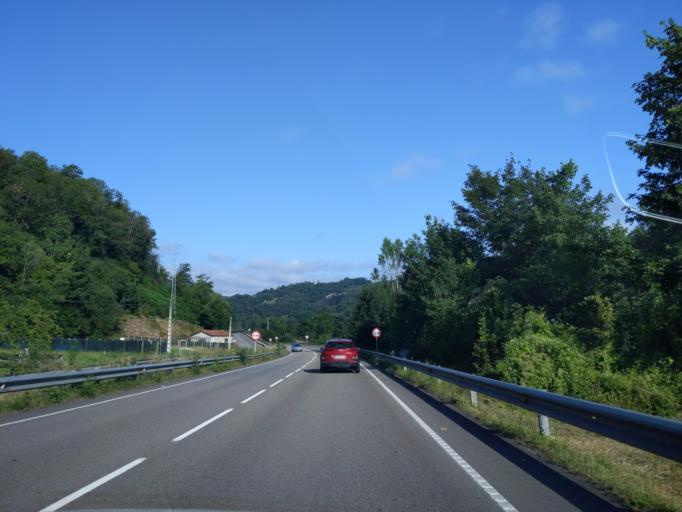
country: ES
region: Asturias
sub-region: Province of Asturias
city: Pola de Laviana
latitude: 43.2341
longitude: -5.5358
